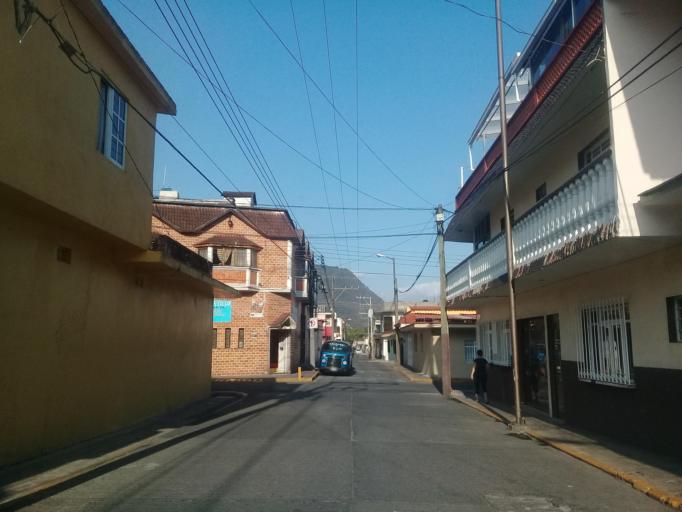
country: MX
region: Veracruz
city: Orizaba
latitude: 18.8555
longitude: -97.1109
